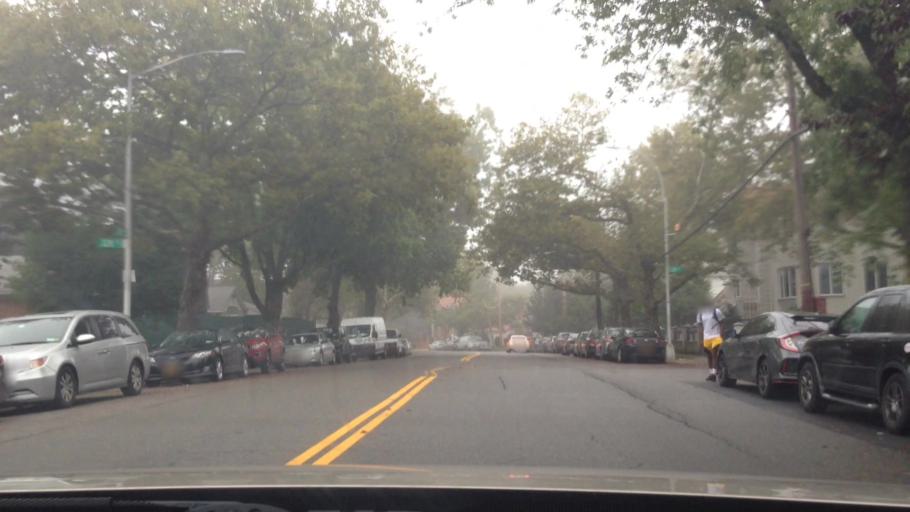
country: US
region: New York
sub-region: Nassau County
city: East Atlantic Beach
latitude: 40.7549
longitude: -73.7528
